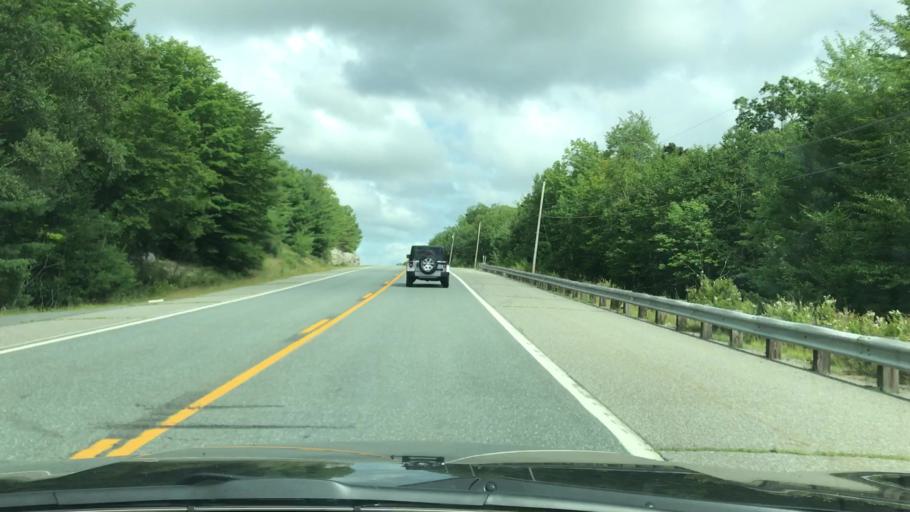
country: US
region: Maine
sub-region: Hancock County
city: Surry
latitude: 44.5646
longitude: -68.6032
